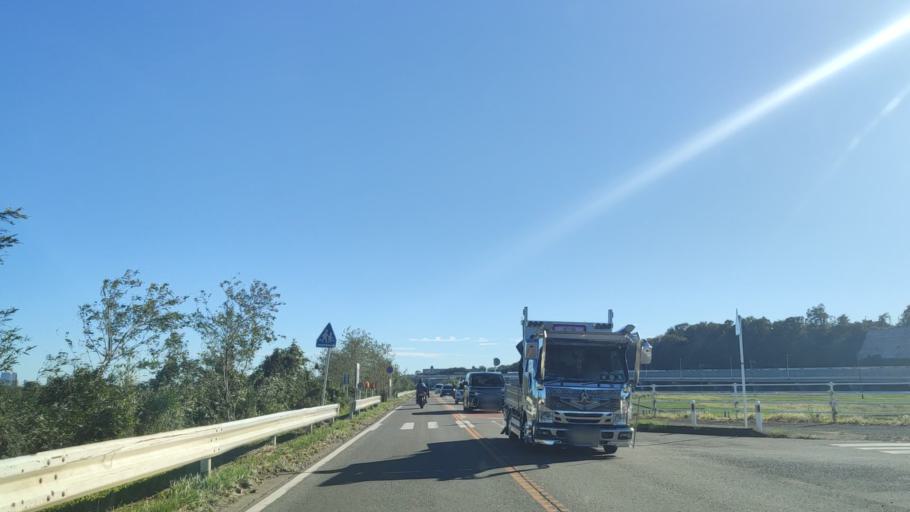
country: JP
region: Kanagawa
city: Zama
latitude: 35.4974
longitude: 139.3708
